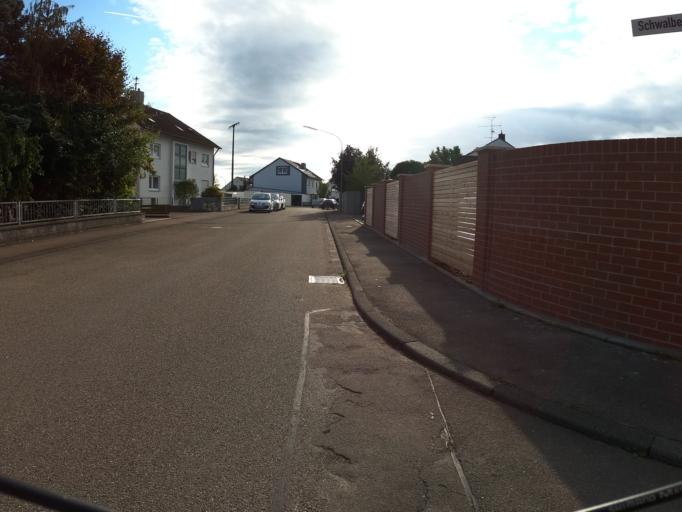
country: DE
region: Bavaria
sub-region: Swabia
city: Nersingen
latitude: 48.4238
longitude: 10.1198
